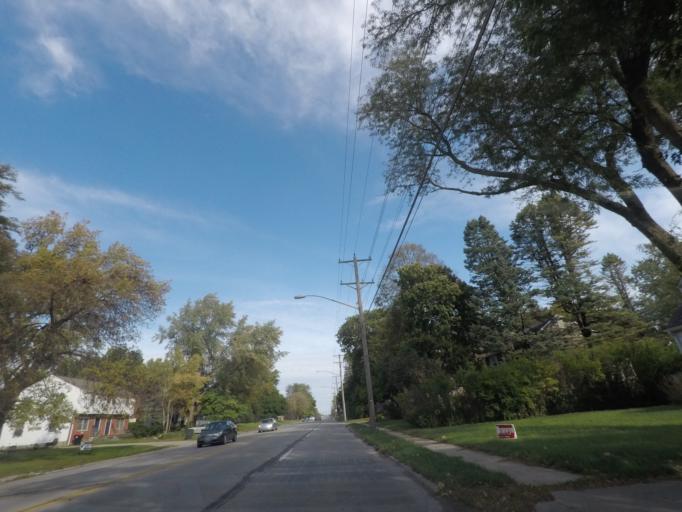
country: US
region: Iowa
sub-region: Story County
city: Ames
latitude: 42.0365
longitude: -93.6203
